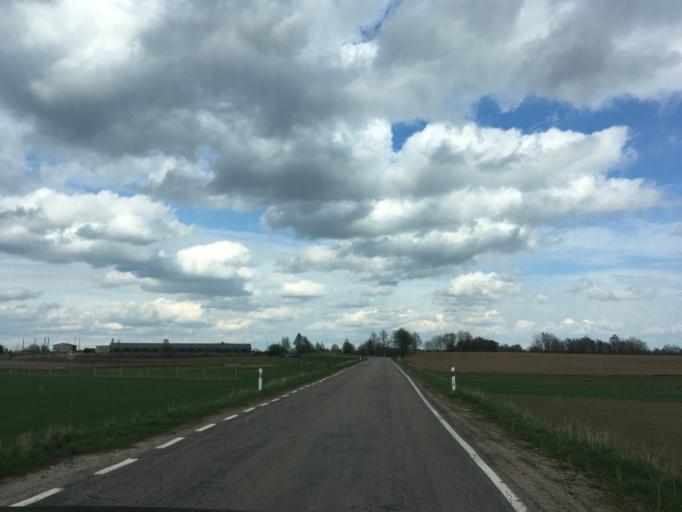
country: LT
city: Virbalis
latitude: 54.3615
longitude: 22.8246
